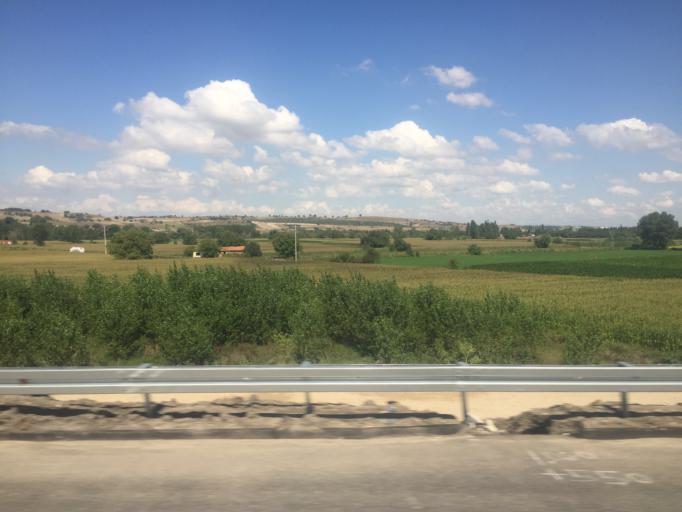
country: TR
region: Balikesir
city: Gobel
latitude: 39.9852
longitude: 28.1829
